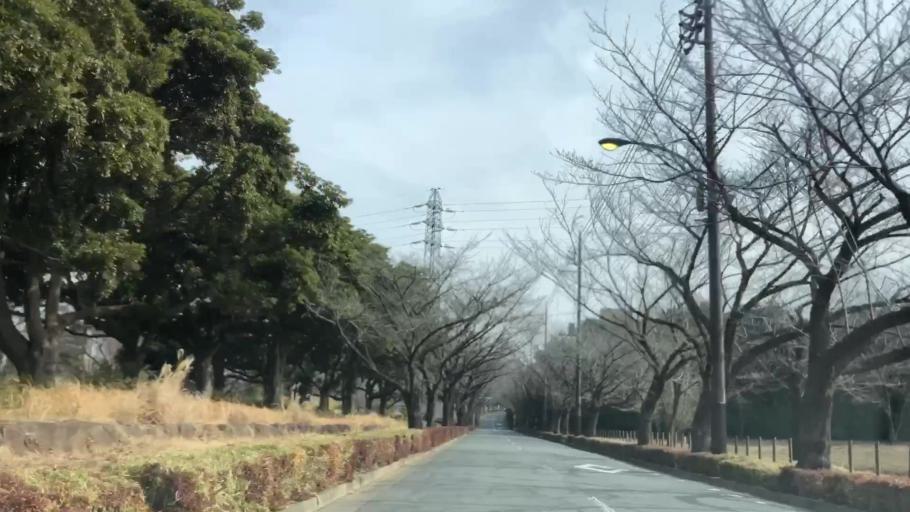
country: JP
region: Saitama
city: Wako
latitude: 35.7758
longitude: 139.6019
